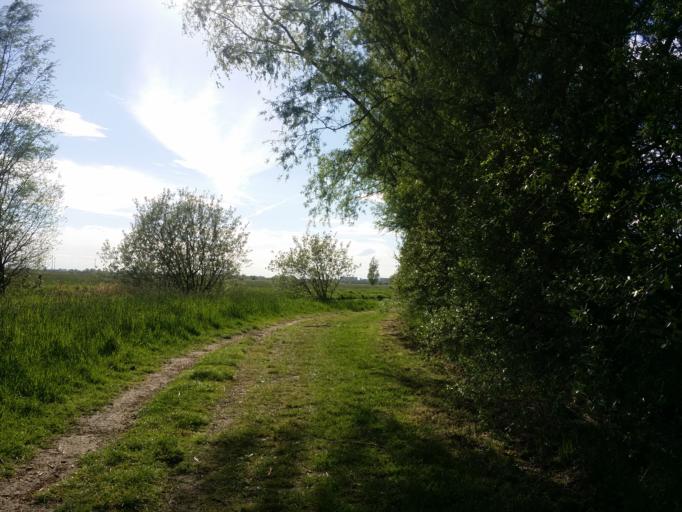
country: DE
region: Lower Saxony
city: Lemwerder
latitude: 53.1557
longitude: 8.6677
